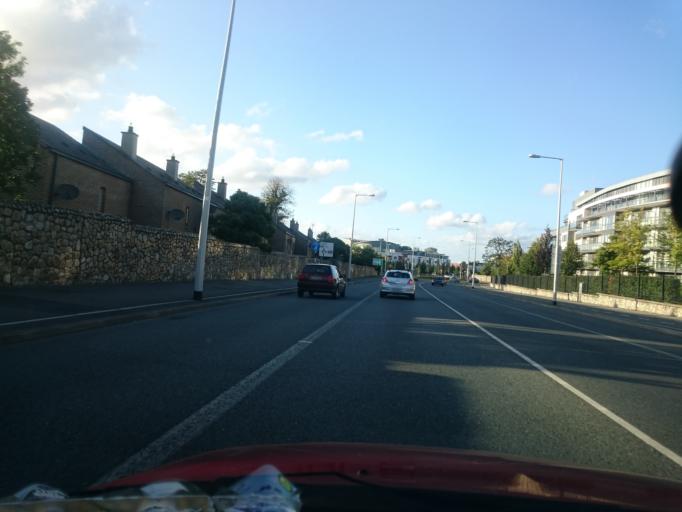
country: IE
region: Leinster
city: Balally
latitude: 53.2803
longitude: -6.2446
